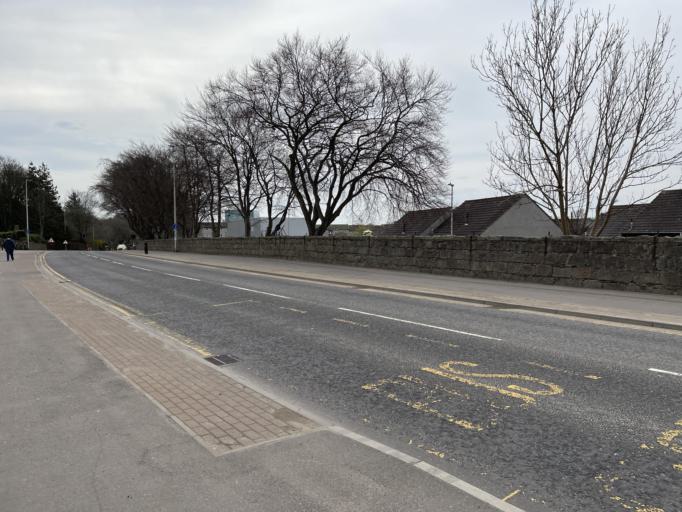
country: GB
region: Scotland
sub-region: Aberdeen City
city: Aberdeen
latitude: 57.1716
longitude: -2.1095
